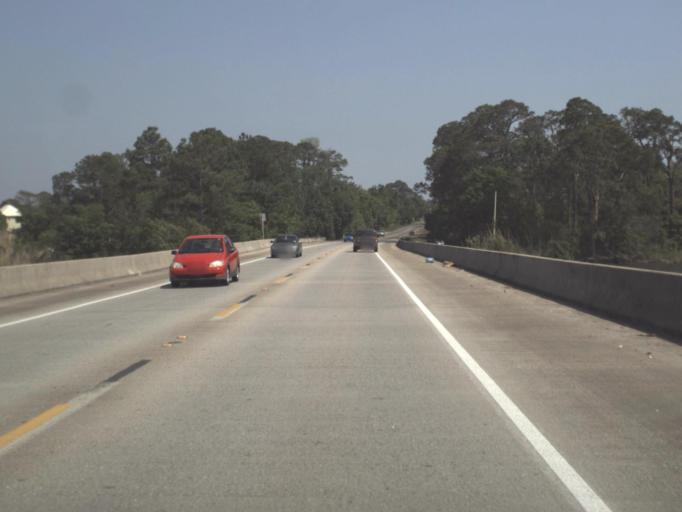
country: US
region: Florida
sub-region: Escambia County
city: Myrtle Grove
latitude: 30.4027
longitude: -87.4269
